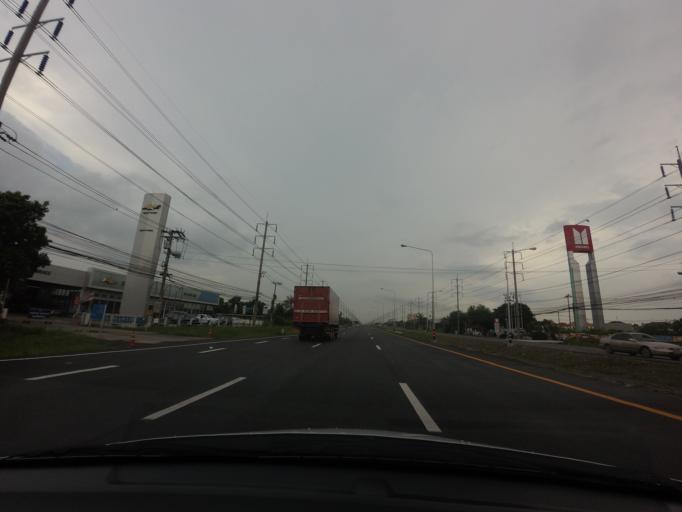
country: TH
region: Bangkok
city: Nong Chok
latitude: 13.8089
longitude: 100.8189
